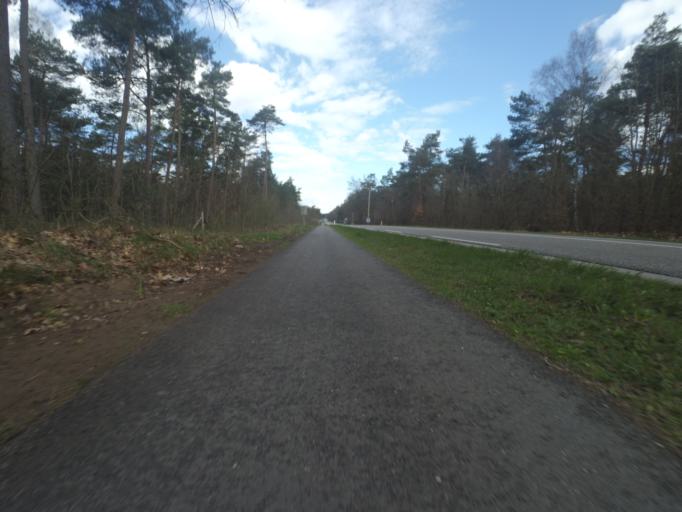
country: NL
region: Gelderland
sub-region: Gemeente Apeldoorn
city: Loenen
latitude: 52.1330
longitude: 6.0025
